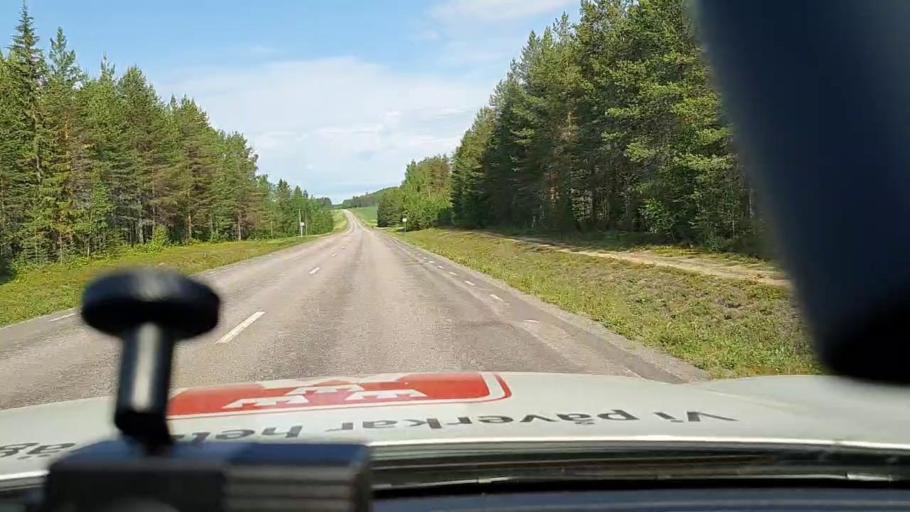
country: SE
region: Norrbotten
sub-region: Bodens Kommun
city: Boden
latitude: 65.9088
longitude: 21.3548
